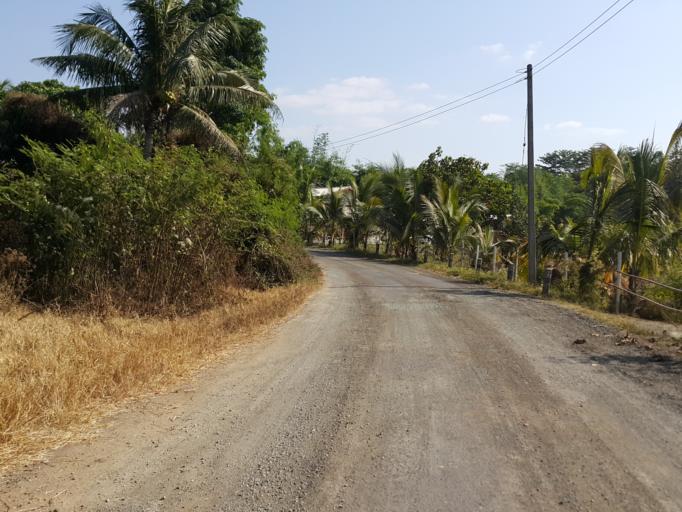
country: TH
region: Chiang Mai
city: Mae On
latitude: 18.8330
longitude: 99.2275
